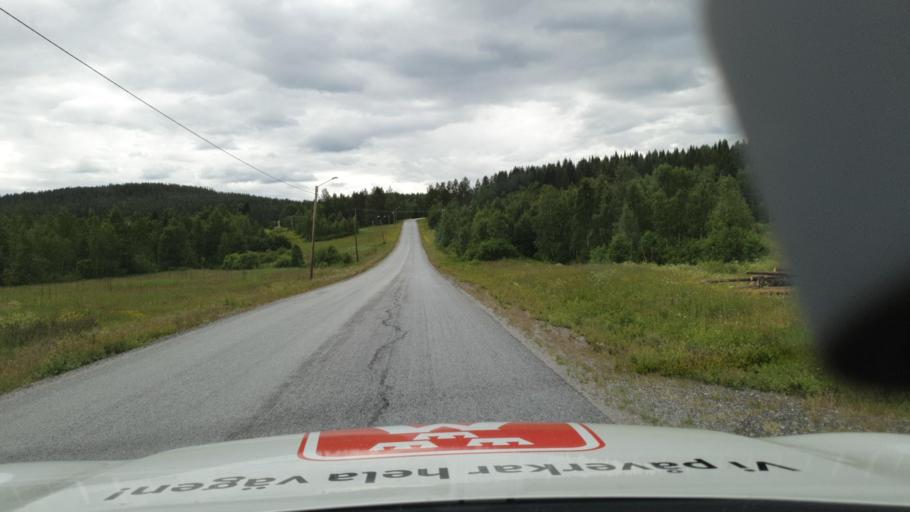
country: SE
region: Vaesterbotten
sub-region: Bjurholms Kommun
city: Bjurholm
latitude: 63.7836
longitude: 19.1620
